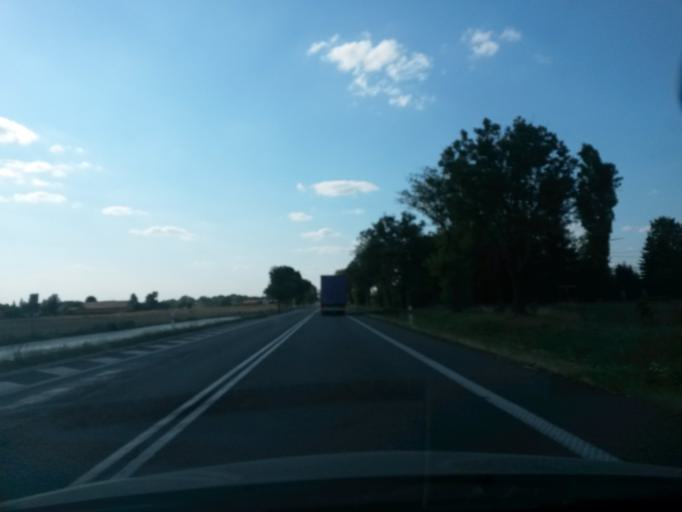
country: PL
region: Masovian Voivodeship
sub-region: Powiat sierpecki
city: Sierpc
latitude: 52.8388
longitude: 19.7323
